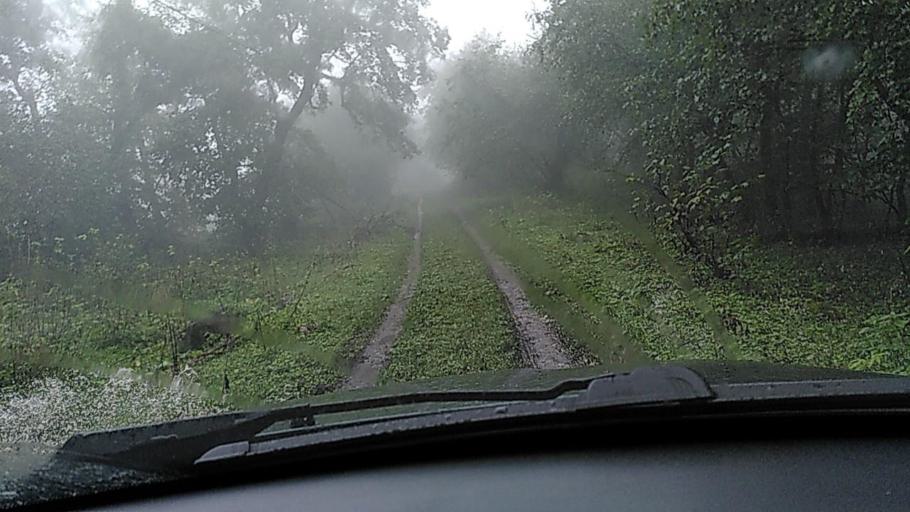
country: RU
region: Kabardino-Balkariya
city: Belaya Rechka
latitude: 43.3573
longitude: 43.3965
